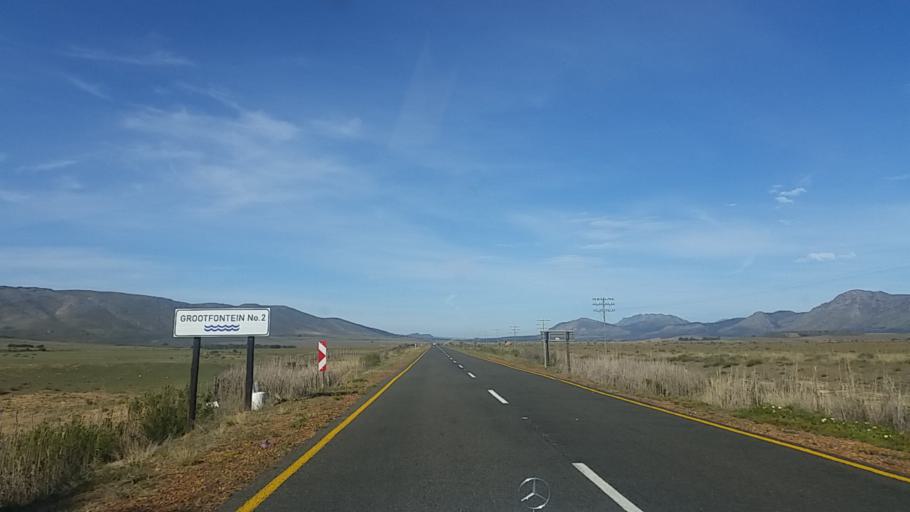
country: ZA
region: Western Cape
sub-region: Eden District Municipality
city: George
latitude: -33.8128
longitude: 22.5303
